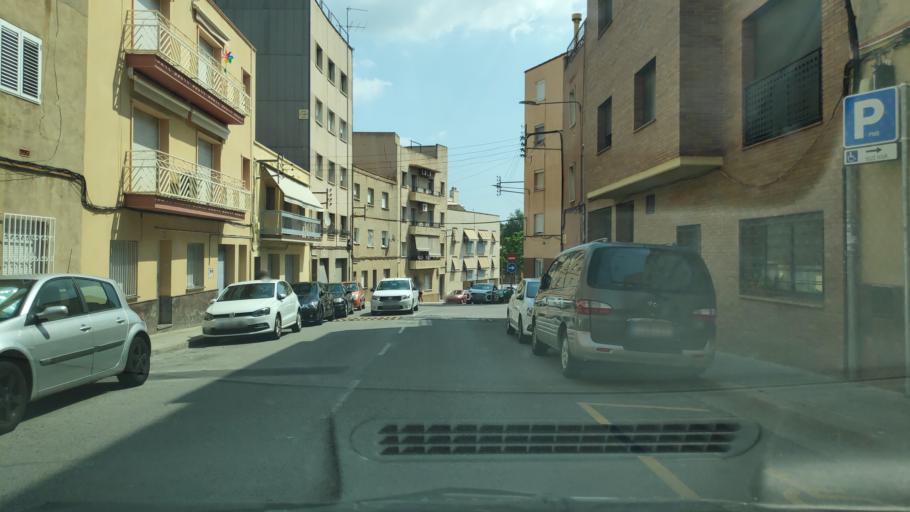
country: ES
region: Catalonia
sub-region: Provincia de Barcelona
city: Sant Quirze del Valles
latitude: 41.5503
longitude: 2.0876
